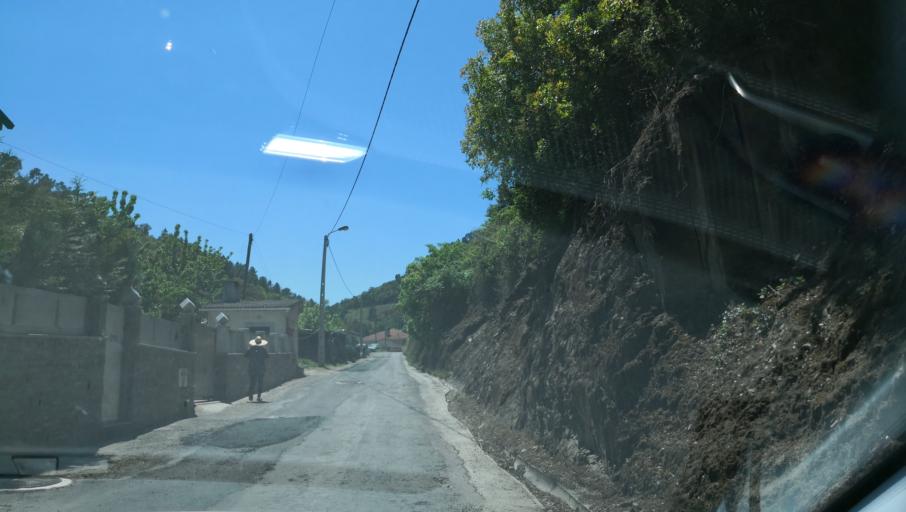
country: PT
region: Vila Real
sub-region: Santa Marta de Penaguiao
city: Santa Marta de Penaguiao
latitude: 41.2212
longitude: -7.7225
